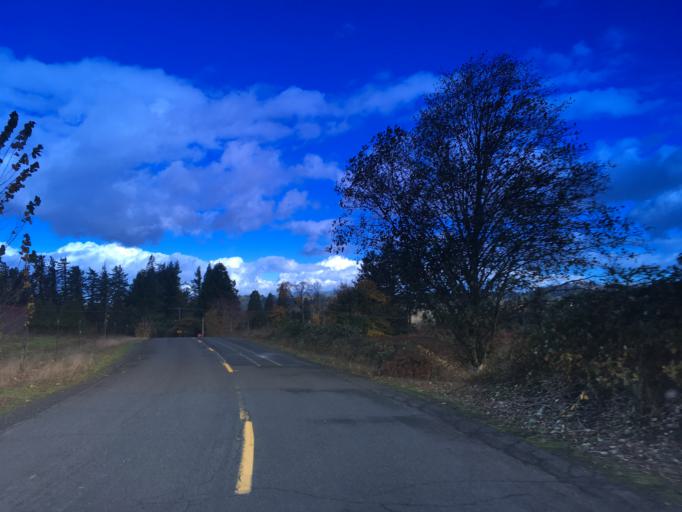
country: US
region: Oregon
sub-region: Multnomah County
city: Troutdale
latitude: 45.5072
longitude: -122.3729
